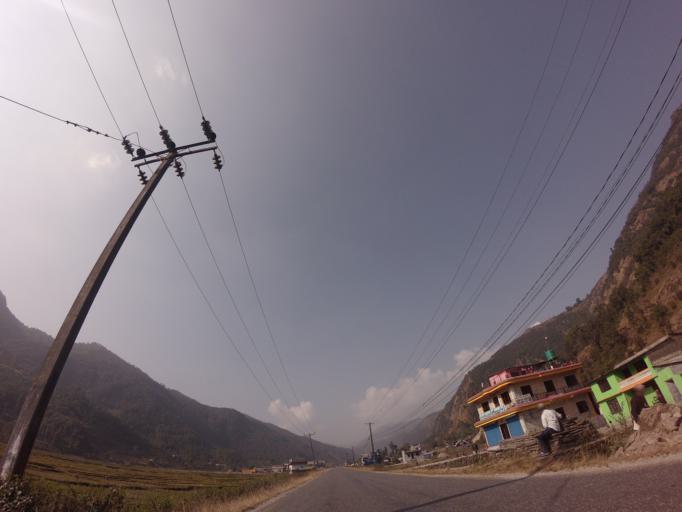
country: NP
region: Western Region
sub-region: Gandaki Zone
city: Pokhara
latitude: 28.2851
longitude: 83.9081
